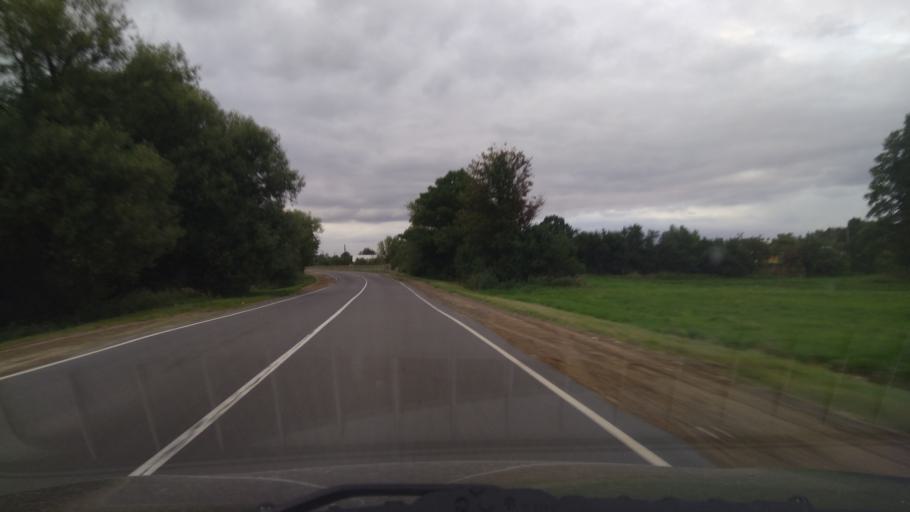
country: BY
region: Brest
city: Byaroza
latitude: 52.4195
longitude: 24.9804
